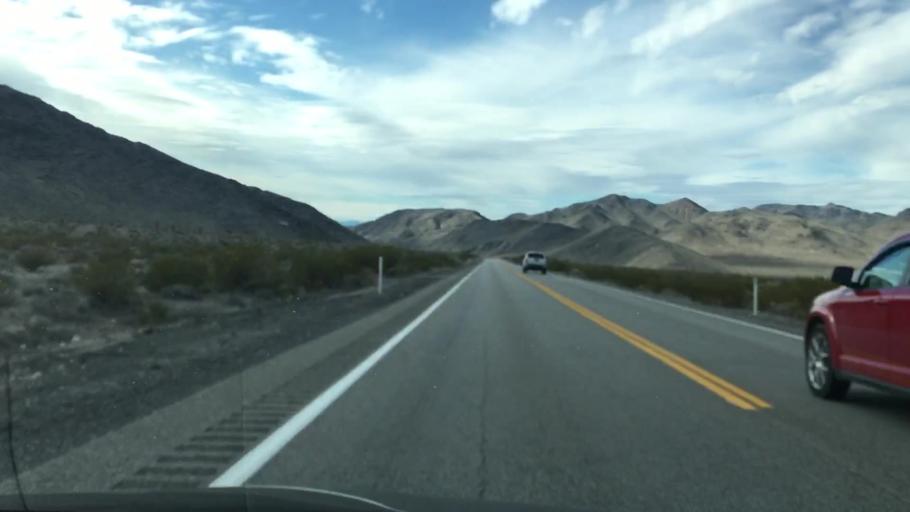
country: US
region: Nevada
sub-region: Nye County
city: Pahrump
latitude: 36.5904
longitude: -116.0382
